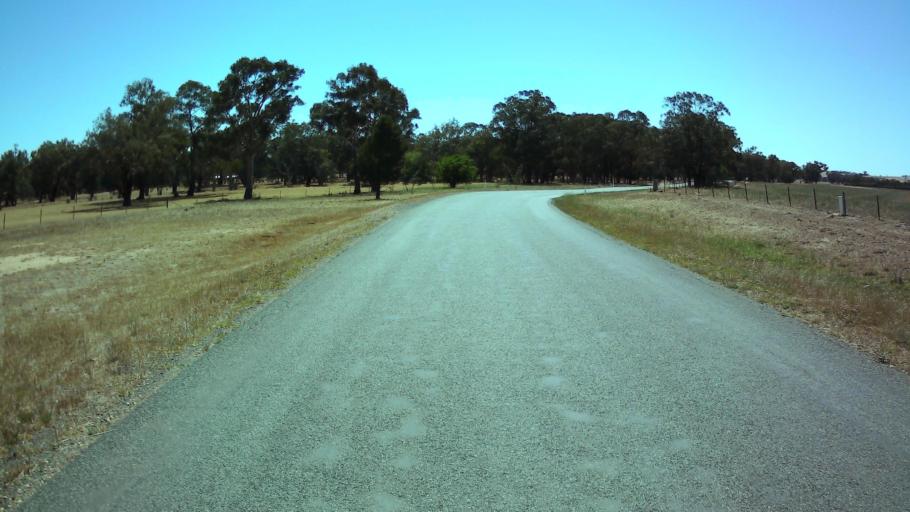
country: AU
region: New South Wales
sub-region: Weddin
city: Grenfell
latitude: -34.0004
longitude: 148.3913
